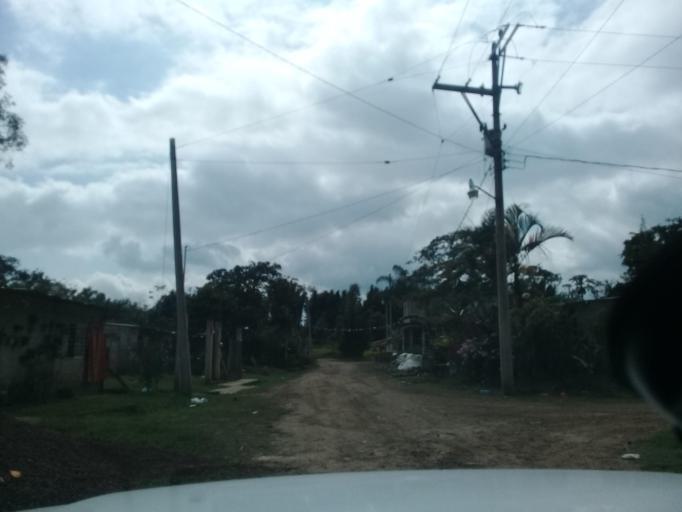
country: MX
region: Veracruz
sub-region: Xalapa
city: Fraccionamiento las Fuentes
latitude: 19.4741
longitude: -96.8762
